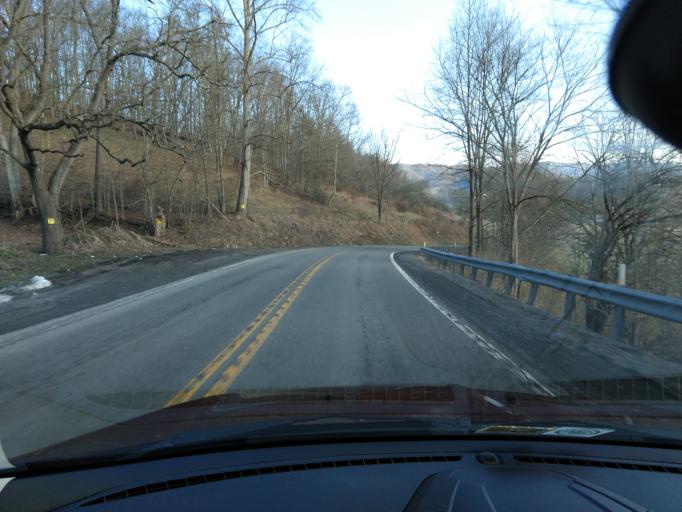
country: US
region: West Virginia
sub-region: Pocahontas County
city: Marlinton
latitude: 38.1228
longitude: -80.2371
